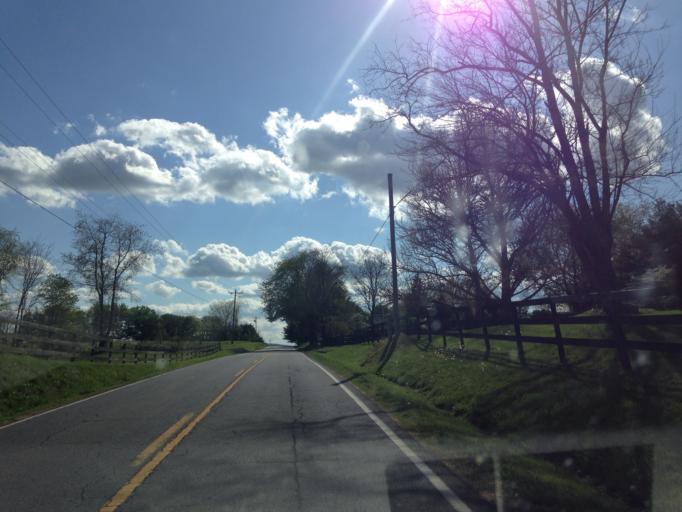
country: US
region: Virginia
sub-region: Loudoun County
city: Lovettsville
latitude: 39.2685
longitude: -77.6210
